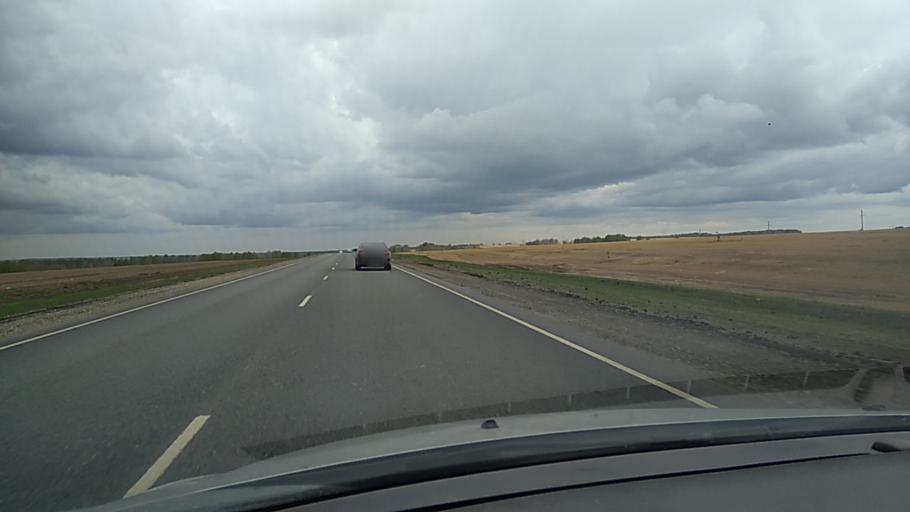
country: RU
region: Kurgan
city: Dalmatovo
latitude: 56.2892
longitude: 62.7769
